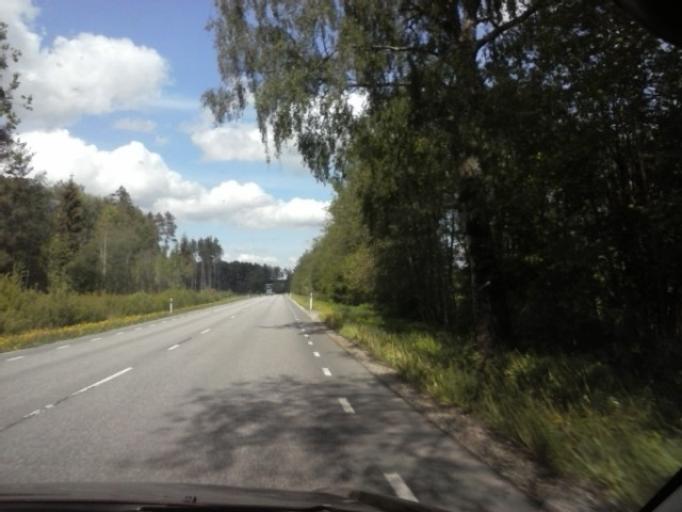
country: EE
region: Raplamaa
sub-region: Rapla vald
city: Rapla
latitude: 58.9608
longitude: 24.7056
